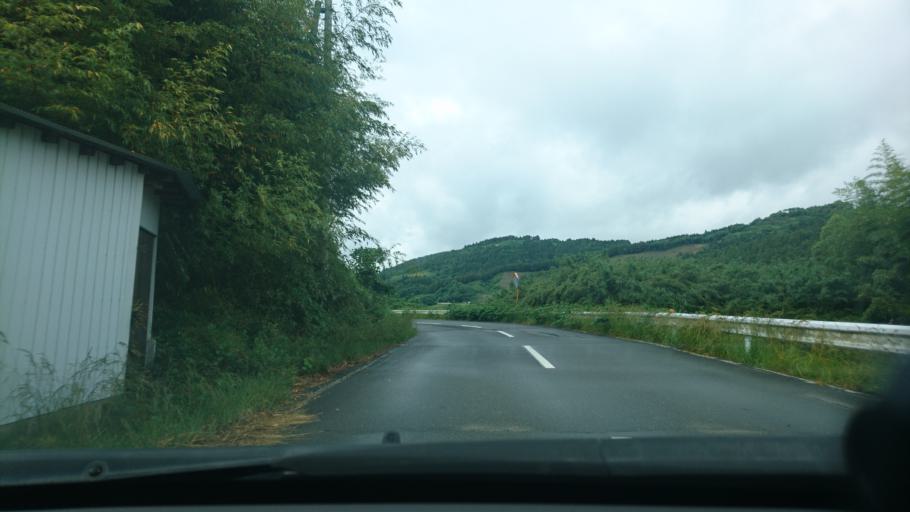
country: JP
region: Miyagi
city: Wakuya
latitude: 38.6647
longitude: 141.2838
